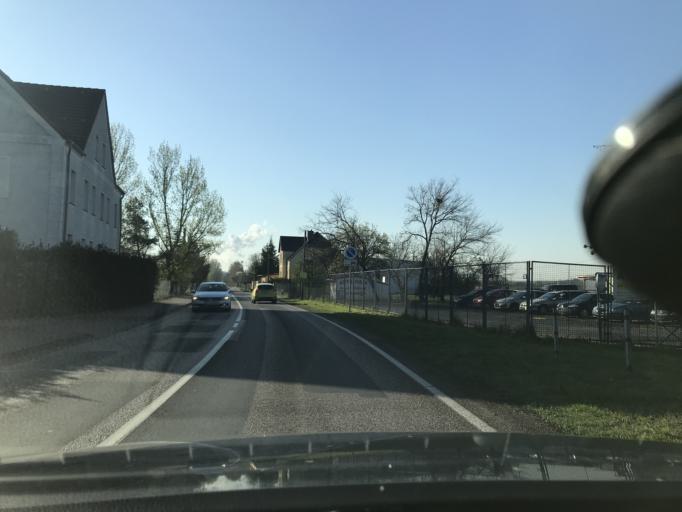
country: DE
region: Saxony-Anhalt
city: Holleben
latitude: 51.4328
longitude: 11.9039
